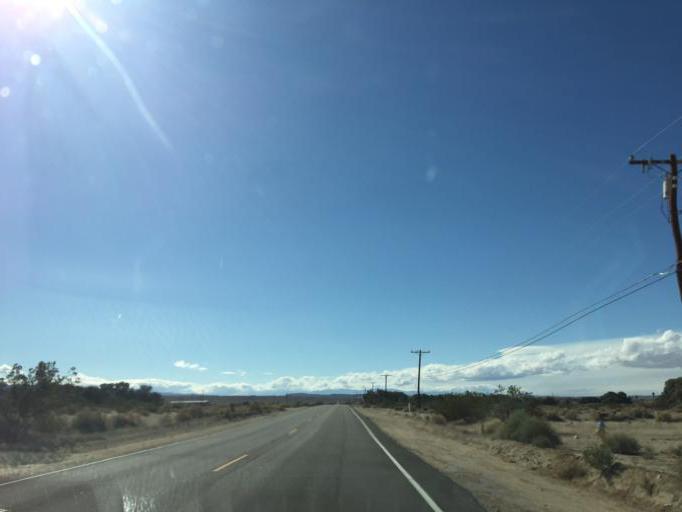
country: US
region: California
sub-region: San Bernardino County
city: Twentynine Palms
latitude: 34.1651
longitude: -116.0306
